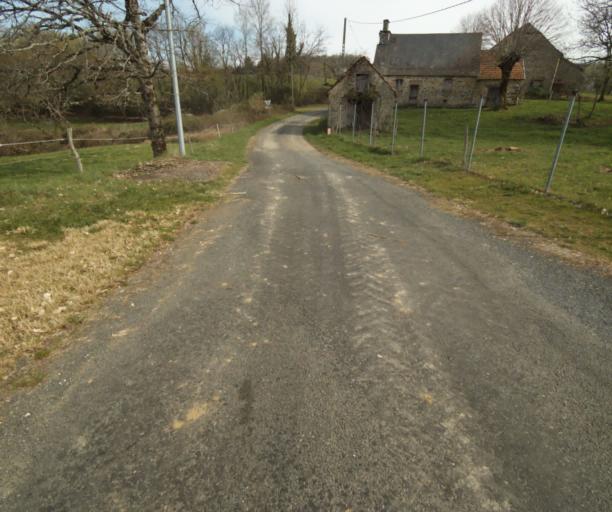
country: FR
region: Limousin
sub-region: Departement de la Correze
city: Correze
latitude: 45.3906
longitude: 1.8221
